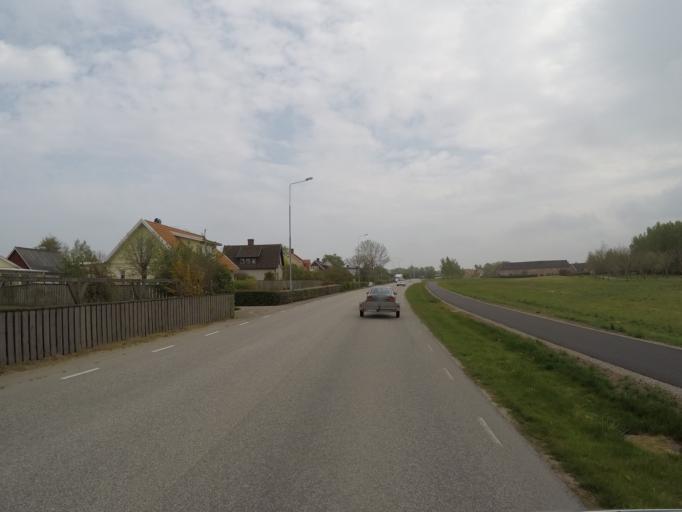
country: SE
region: Halland
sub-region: Laholms Kommun
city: Laholm
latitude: 56.5066
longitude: 13.0583
